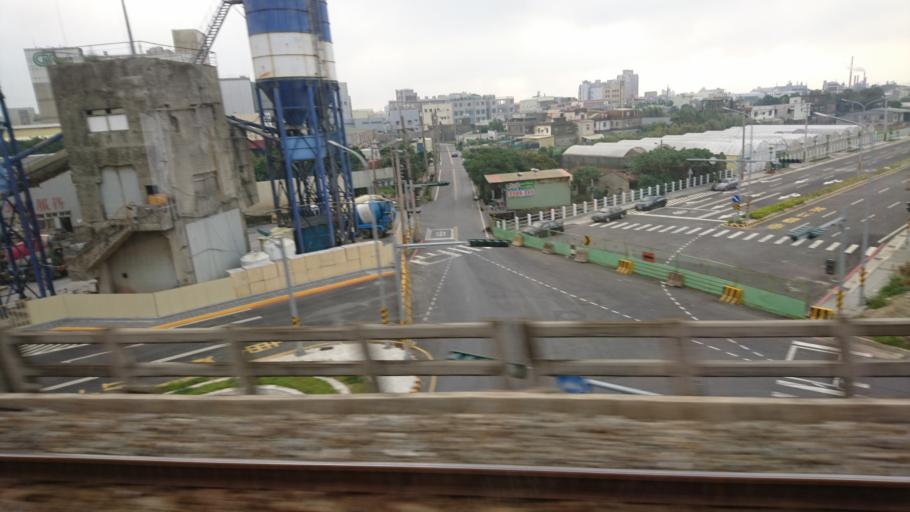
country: TW
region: Taiwan
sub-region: Hsinchu
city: Zhubei
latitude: 24.8504
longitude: 121.0134
